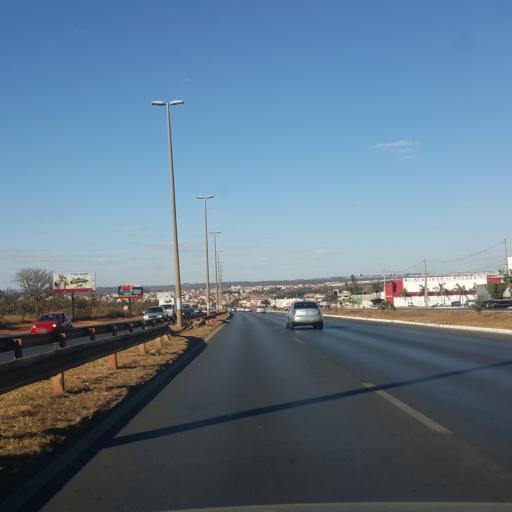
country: BR
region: Federal District
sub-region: Brasilia
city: Brasilia
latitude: -15.7896
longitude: -48.0199
